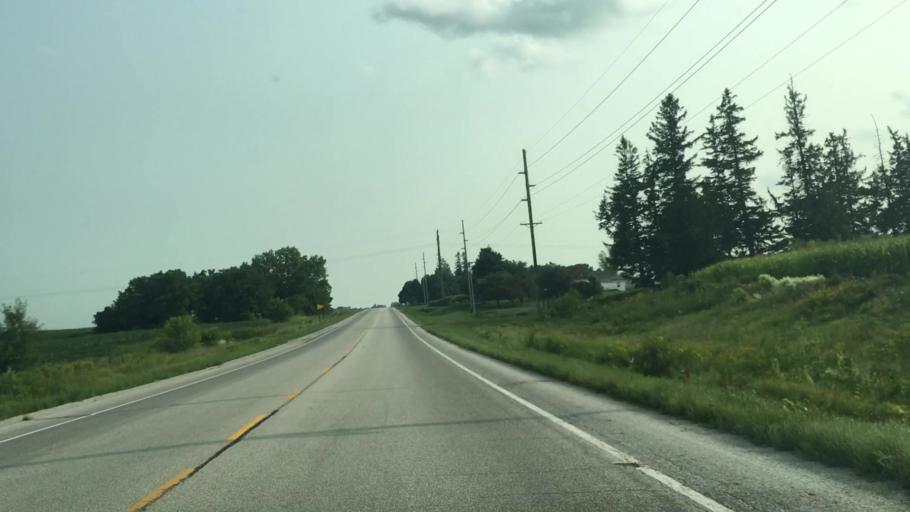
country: US
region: Minnesota
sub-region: Fillmore County
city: Harmony
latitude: 43.5534
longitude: -91.9297
